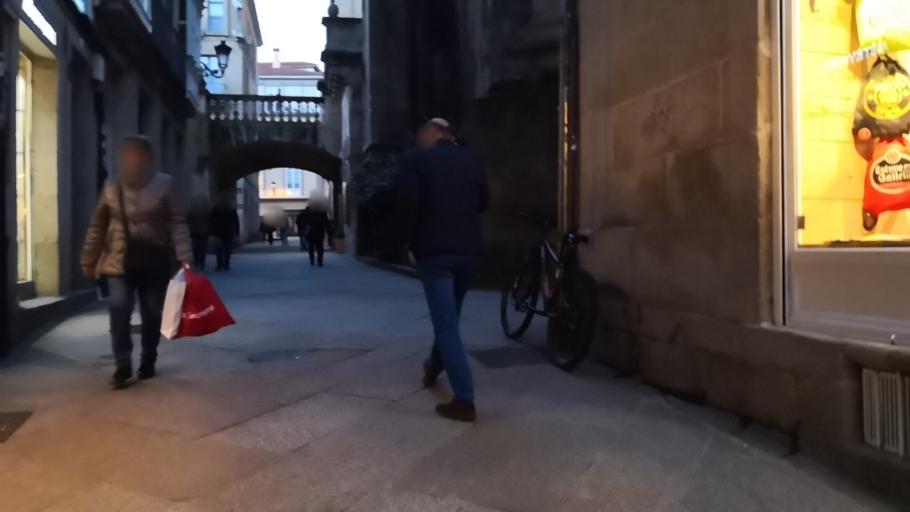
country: ES
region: Galicia
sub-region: Provincia de Ourense
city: Ourense
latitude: 42.3362
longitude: -7.8635
